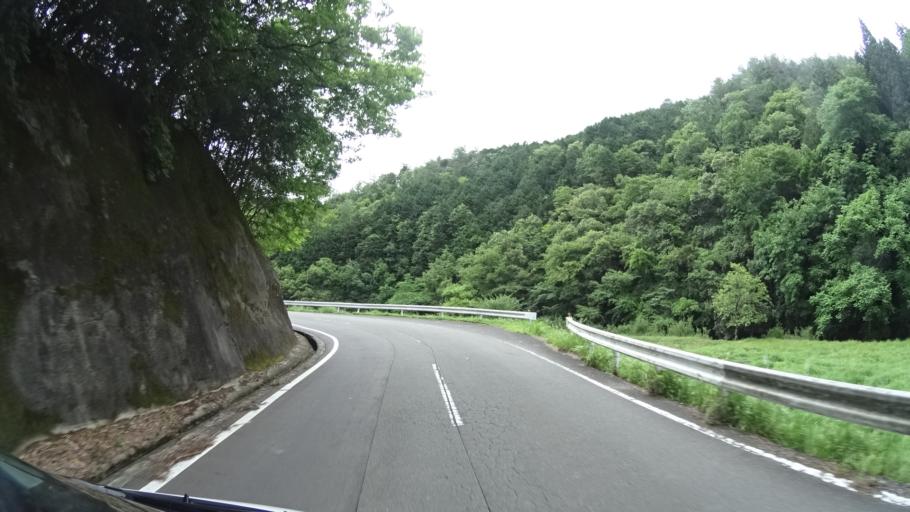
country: JP
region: Hyogo
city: Sasayama
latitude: 35.0648
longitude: 135.3994
